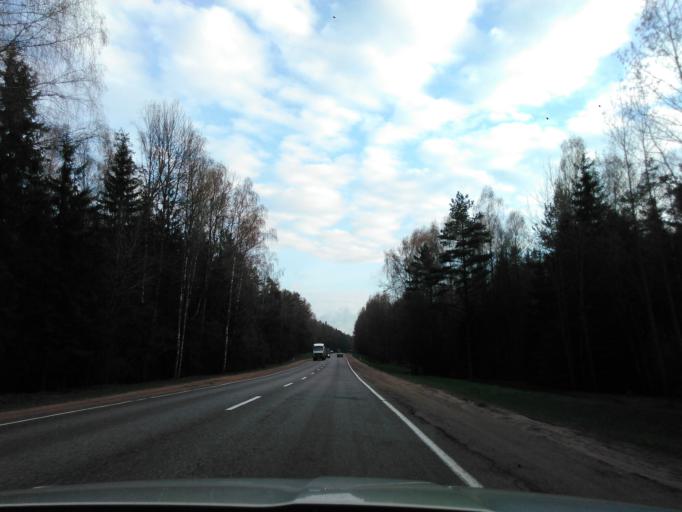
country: BY
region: Minsk
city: Lahoysk
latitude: 54.3145
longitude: 27.8754
